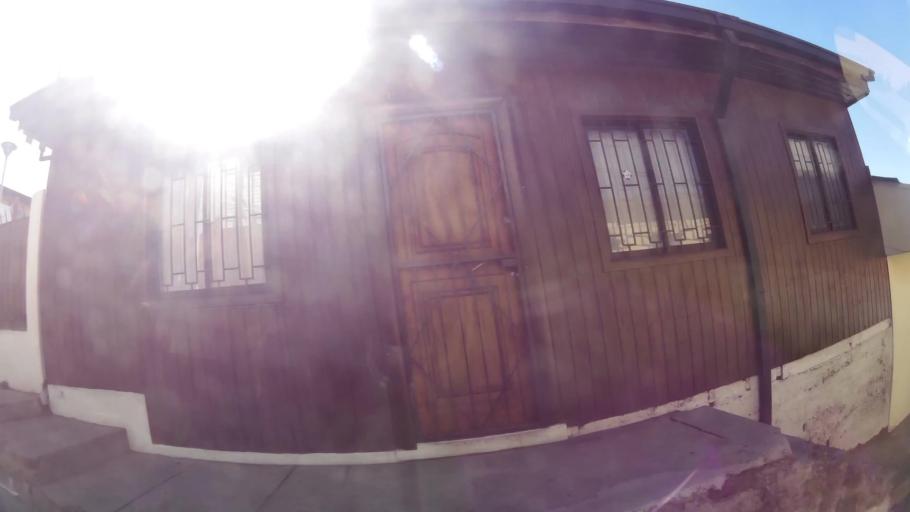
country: CL
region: Valparaiso
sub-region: Provincia de Valparaiso
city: Valparaiso
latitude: -33.0550
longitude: -71.6169
